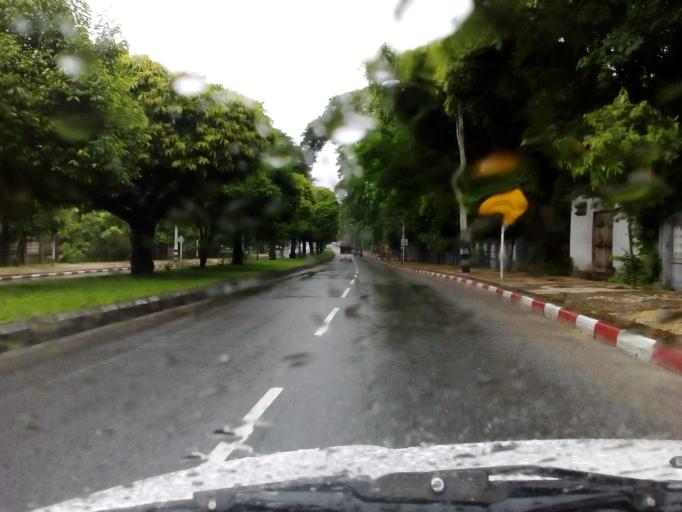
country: MM
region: Yangon
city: Yangon
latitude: 16.7912
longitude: 96.1484
